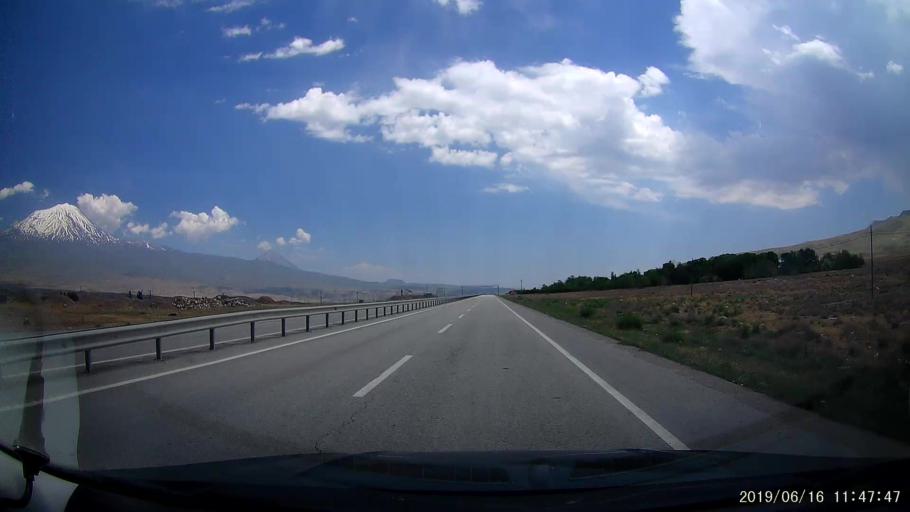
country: TR
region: Agri
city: Dogubayazit
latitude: 39.5583
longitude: 44.1338
